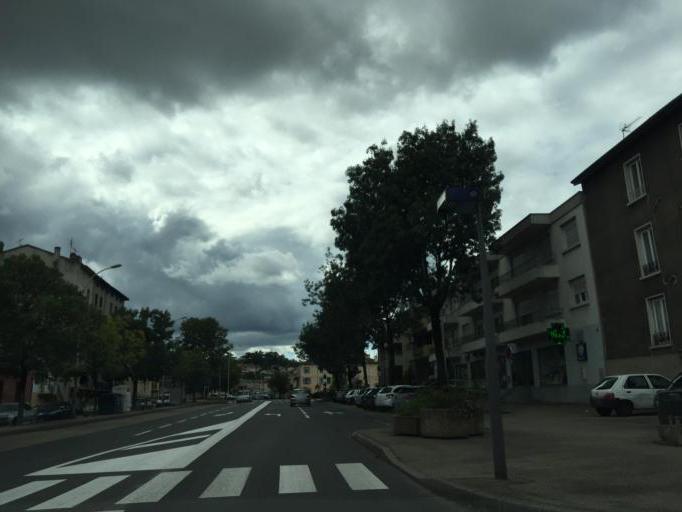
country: FR
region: Rhone-Alpes
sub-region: Departement de la Loire
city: Rive-de-Gier
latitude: 45.5277
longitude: 4.6139
